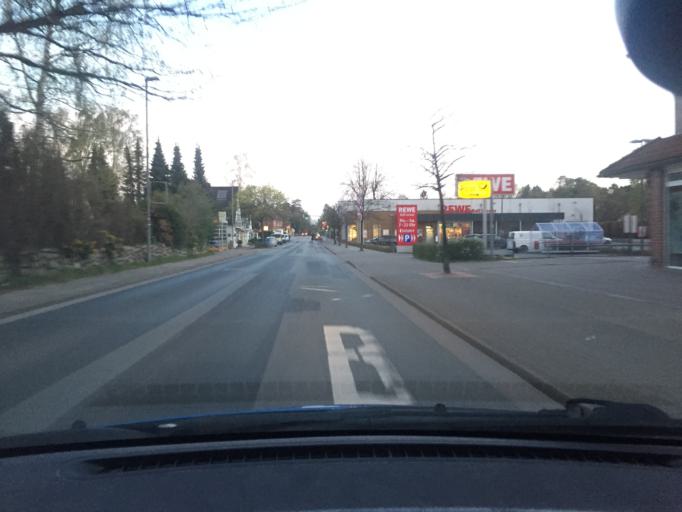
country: DE
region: Lower Saxony
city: Buchholz in der Nordheide
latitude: 53.2876
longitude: 9.8709
